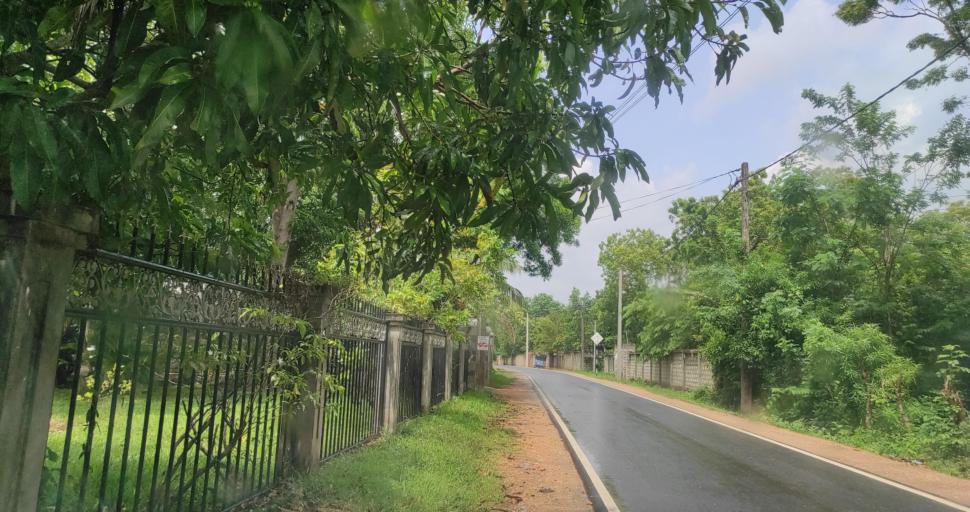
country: LK
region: Eastern Province
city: Trincomalee
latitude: 8.3709
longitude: 81.0128
